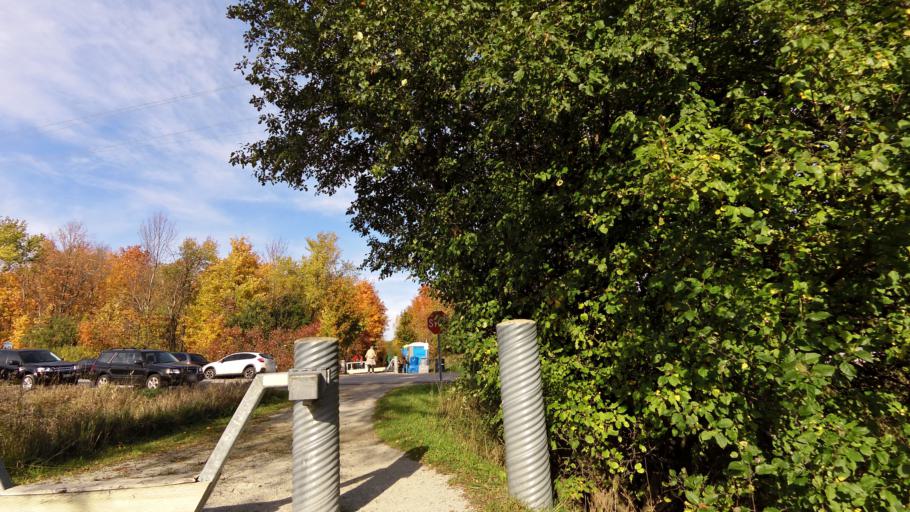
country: CA
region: Ontario
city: Orangeville
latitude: 43.8129
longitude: -80.0288
